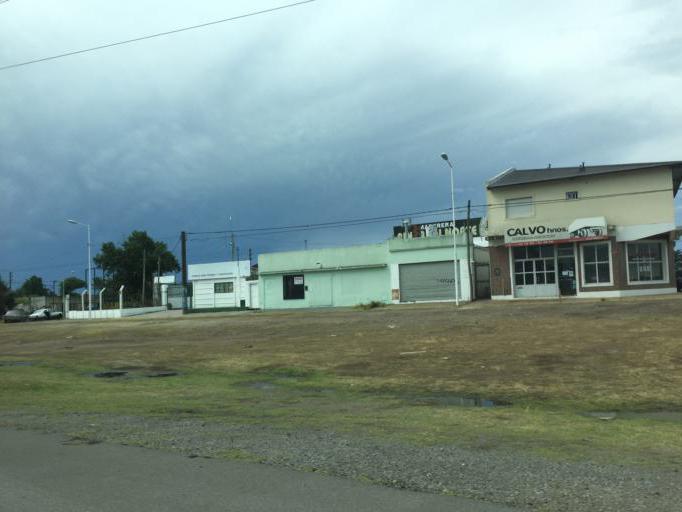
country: AR
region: Buenos Aires
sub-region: Partido de Tandil
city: Tandil
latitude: -37.3069
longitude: -59.1200
